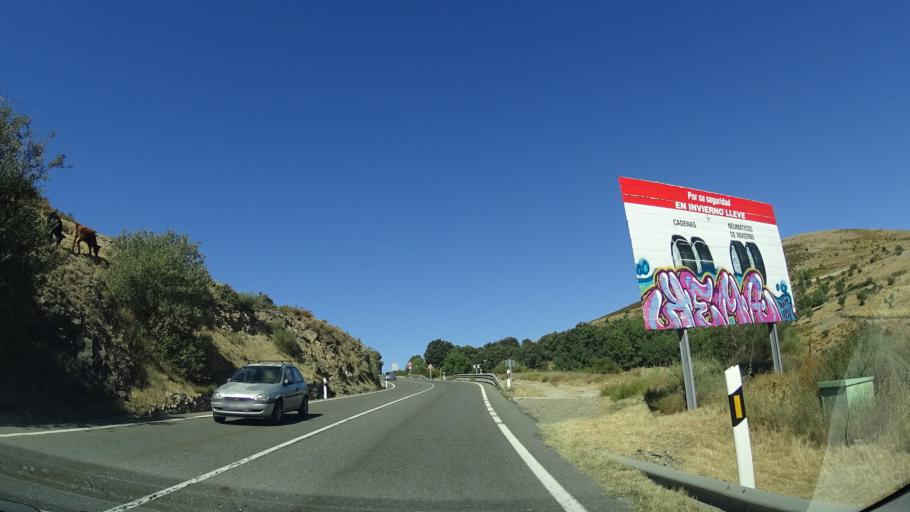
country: ES
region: Madrid
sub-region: Provincia de Madrid
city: Zarzalejo
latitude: 40.5664
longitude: -4.2030
